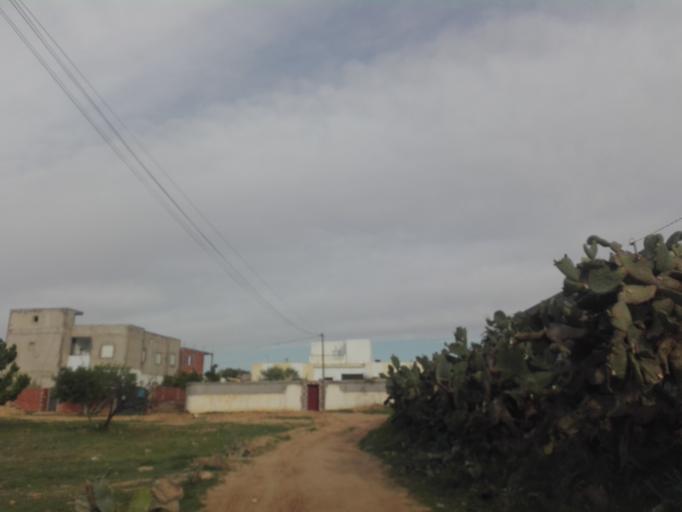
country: TN
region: Safaqis
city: Sfax
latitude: 34.7430
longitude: 10.5225
